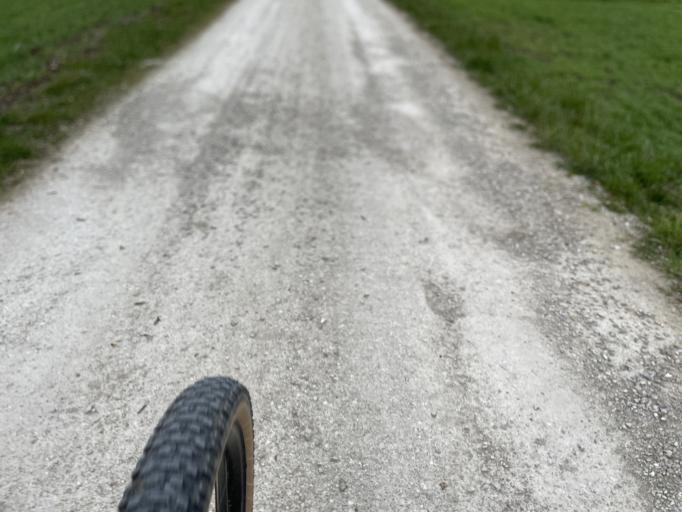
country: CH
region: Bern
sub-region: Bern-Mittelland District
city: Rubigen
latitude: 46.8781
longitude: 7.5335
